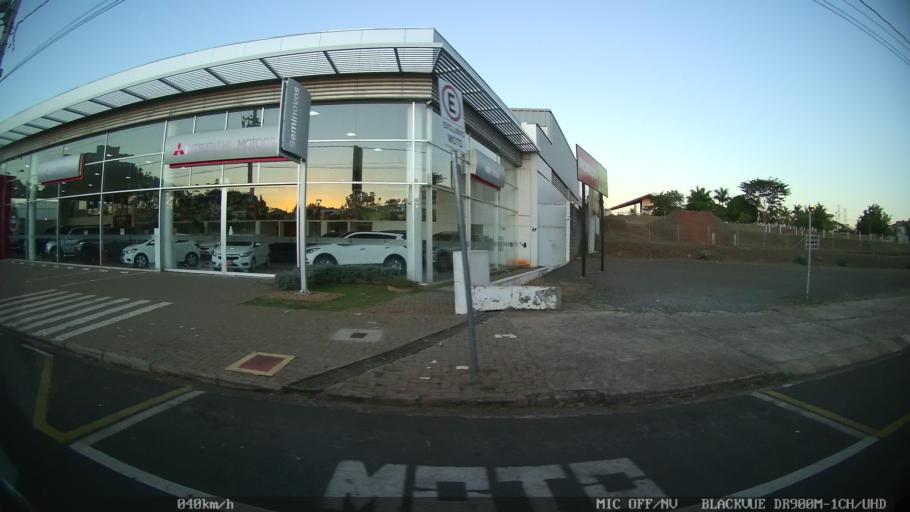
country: BR
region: Sao Paulo
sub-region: Sao Jose Do Rio Preto
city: Sao Jose do Rio Preto
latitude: -20.8415
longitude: -49.3940
